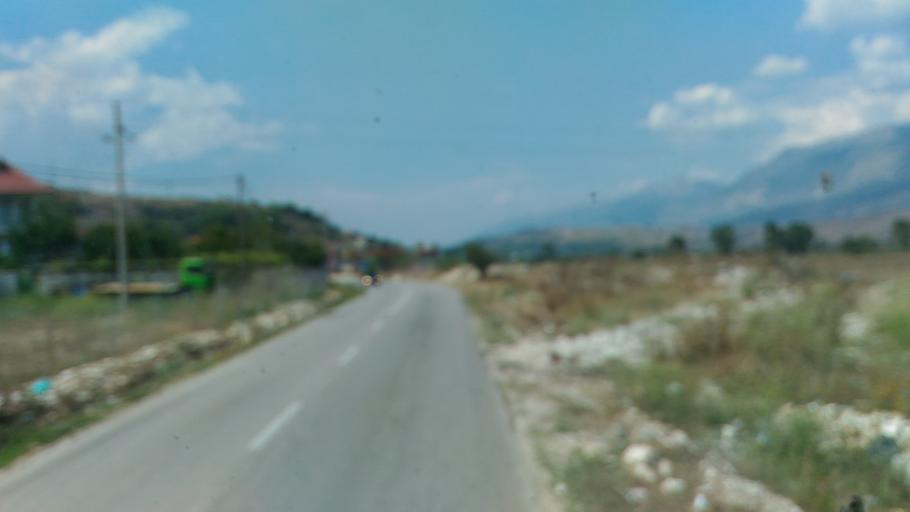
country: AL
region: Gjirokaster
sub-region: Rrethi i Gjirokastres
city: Dervician
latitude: 40.0537
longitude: 20.1767
